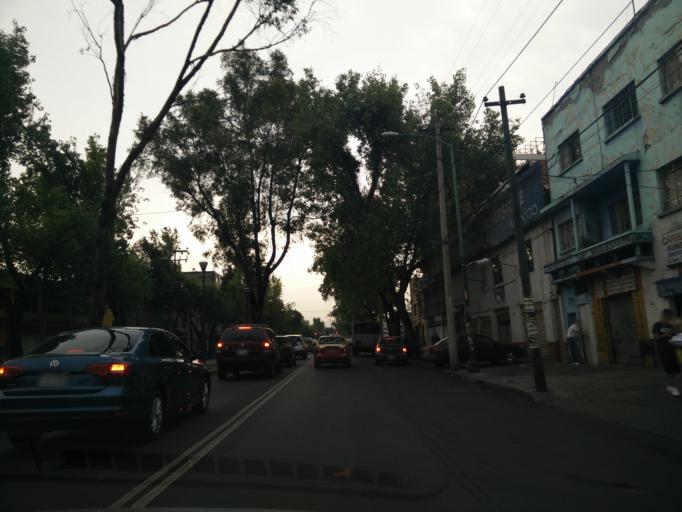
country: MX
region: Mexico City
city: Benito Juarez
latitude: 19.4095
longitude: -99.1493
